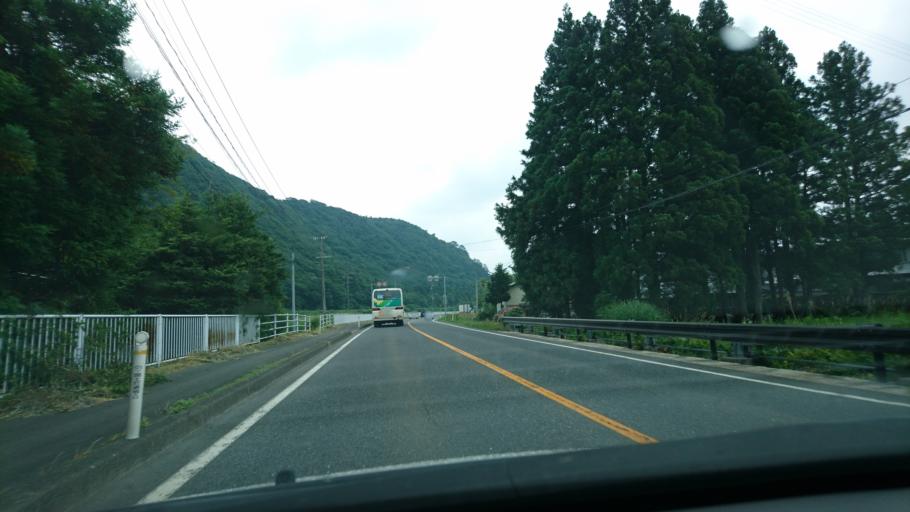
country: JP
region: Miyagi
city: Furukawa
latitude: 38.7250
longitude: 140.7992
